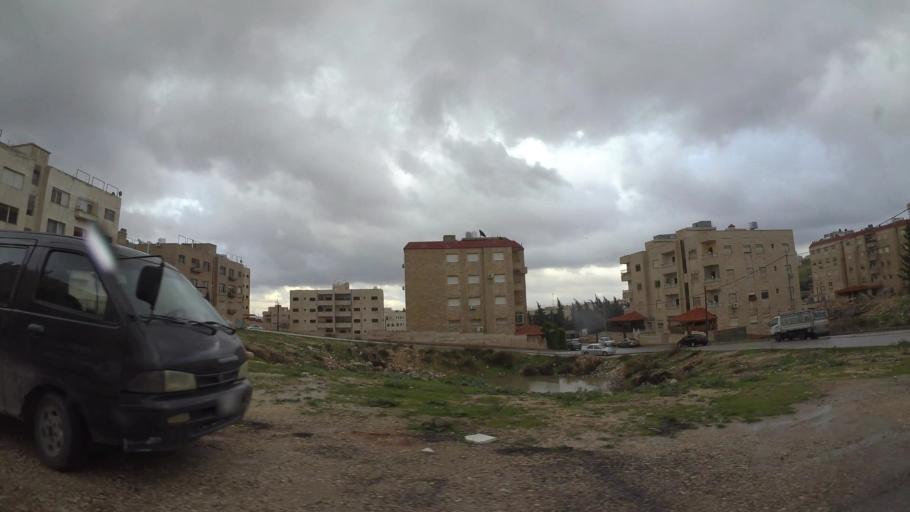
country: JO
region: Amman
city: Amman
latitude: 31.9967
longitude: 35.9242
